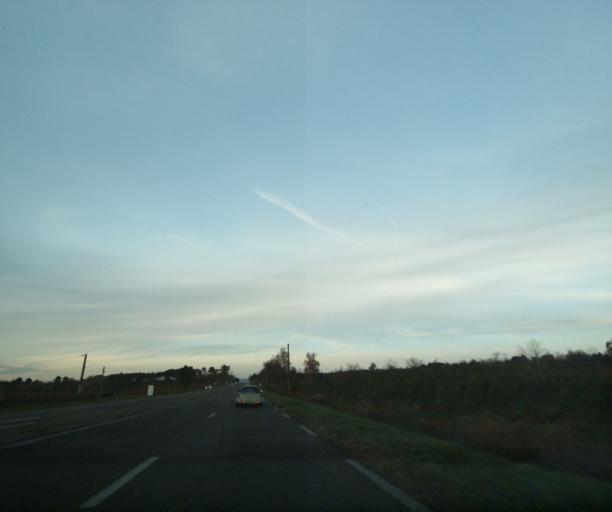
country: FR
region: Aquitaine
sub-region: Departement de la Gironde
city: Langon
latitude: 44.5073
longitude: -0.2385
